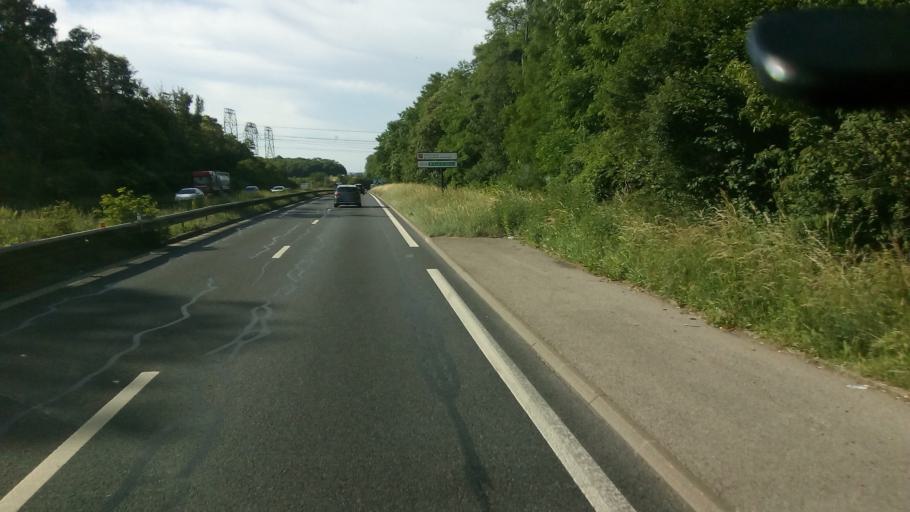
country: FR
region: Ile-de-France
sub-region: Departement de Seine-et-Marne
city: Voisenon
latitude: 48.5636
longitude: 2.6441
